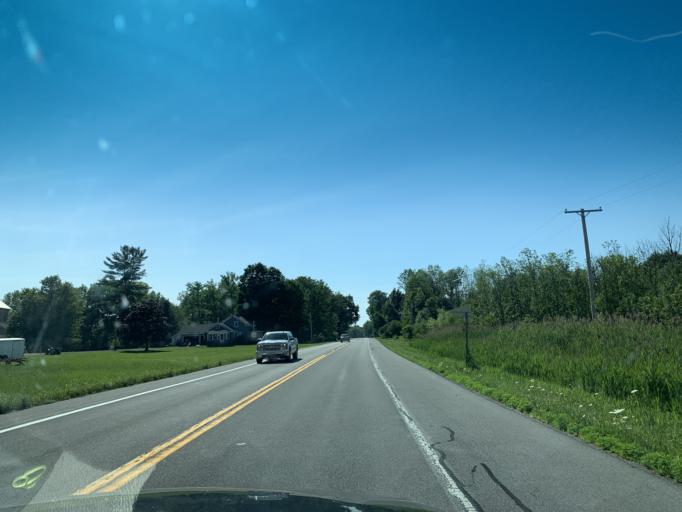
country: US
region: New York
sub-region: Madison County
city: Oneida
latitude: 43.1454
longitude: -75.6538
